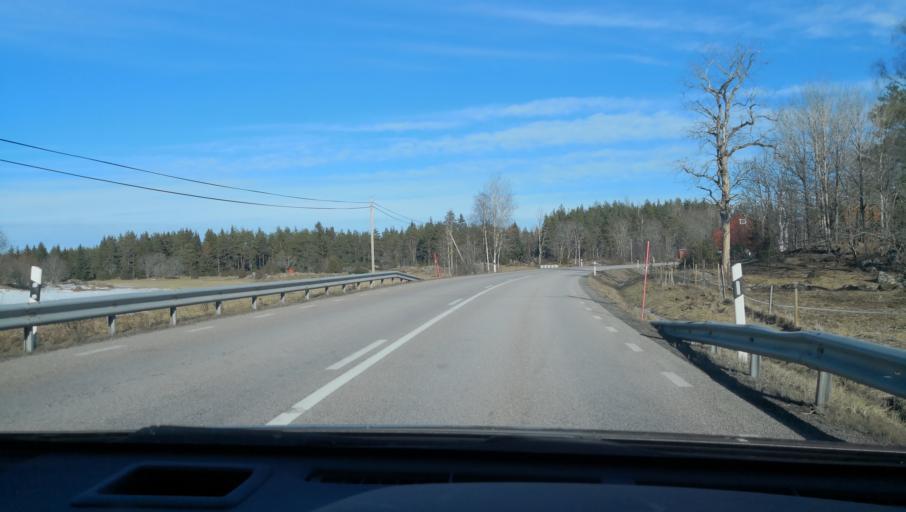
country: SE
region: Uppsala
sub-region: Uppsala Kommun
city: Vattholma
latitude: 60.1199
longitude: 17.7980
